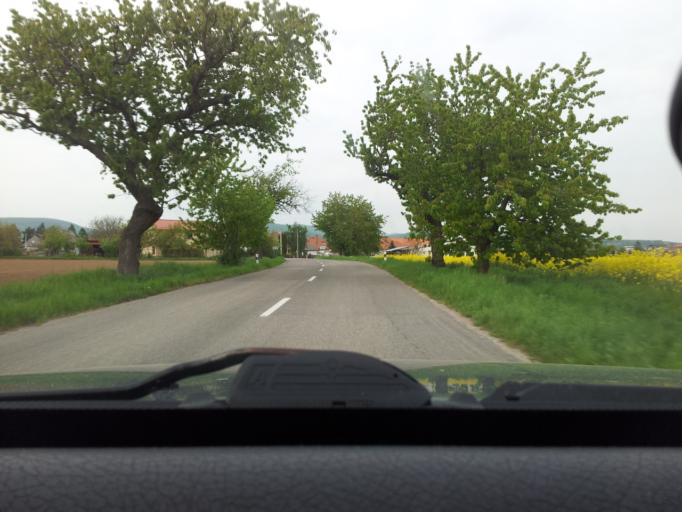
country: SK
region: Nitriansky
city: Tlmace
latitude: 48.2836
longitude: 18.5950
